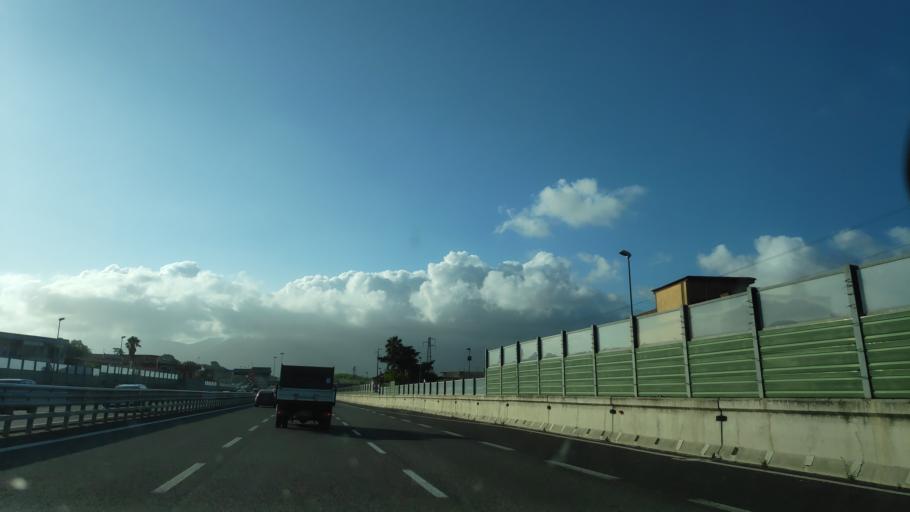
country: IT
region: Campania
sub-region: Provincia di Napoli
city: Torre Annunziata
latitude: 40.7511
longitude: 14.4731
